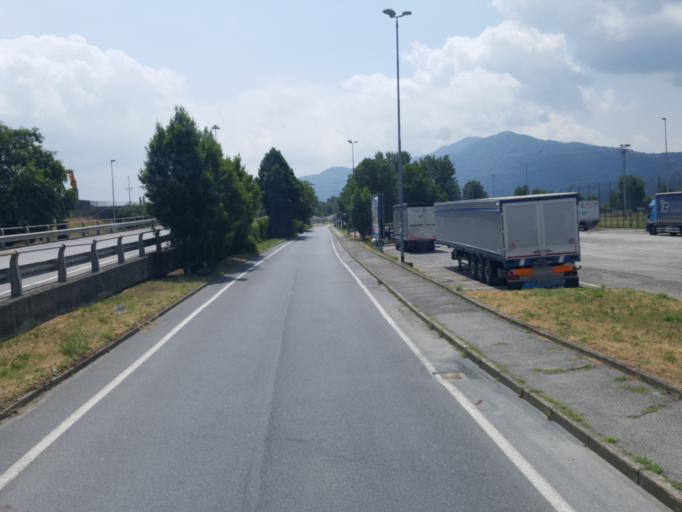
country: IT
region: Lombardy
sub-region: Provincia di Lecco
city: Pescate
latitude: 45.8371
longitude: 9.4077
